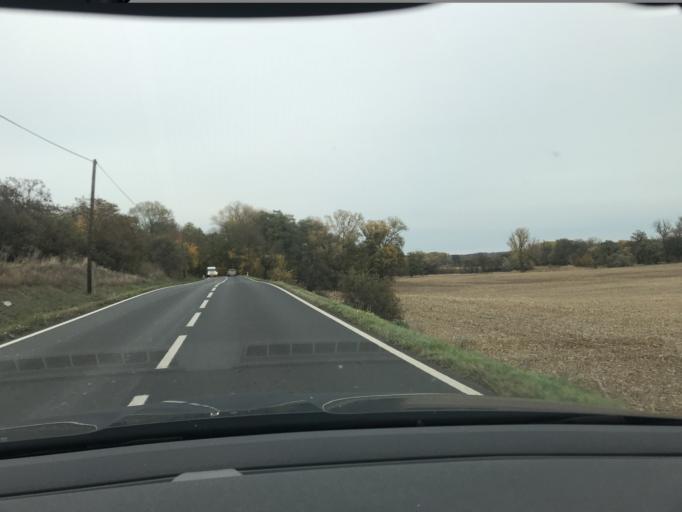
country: CZ
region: Ustecky
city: Budyne nad Ohri
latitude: 50.4137
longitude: 14.0979
